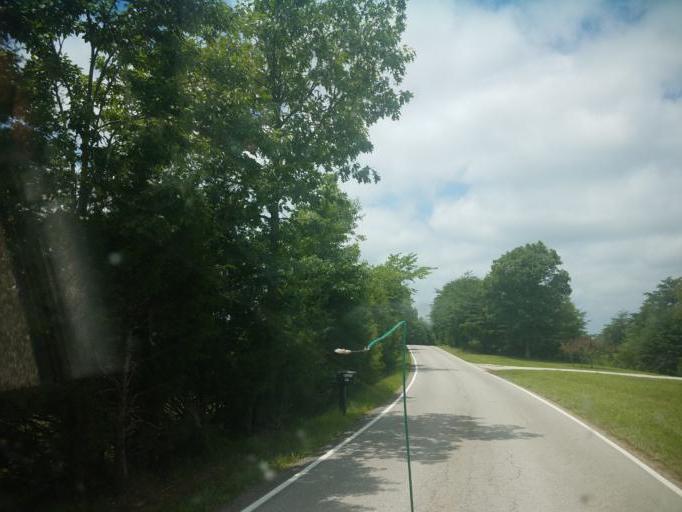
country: US
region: Kentucky
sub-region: Hart County
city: Munfordville
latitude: 37.3321
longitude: -85.9957
